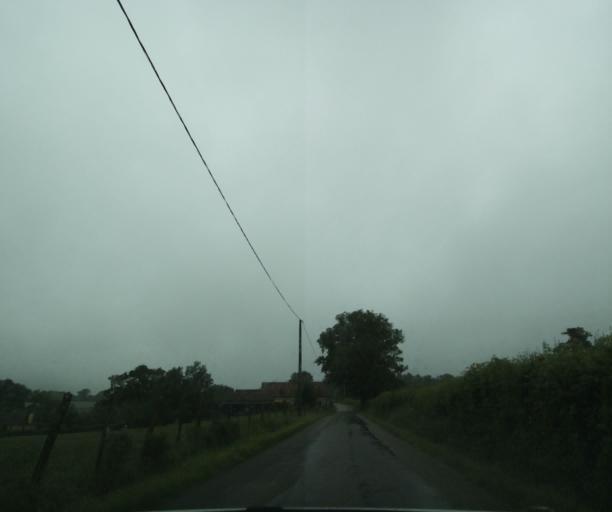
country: FR
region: Bourgogne
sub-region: Departement de Saone-et-Loire
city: Charolles
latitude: 46.4130
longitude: 4.2016
